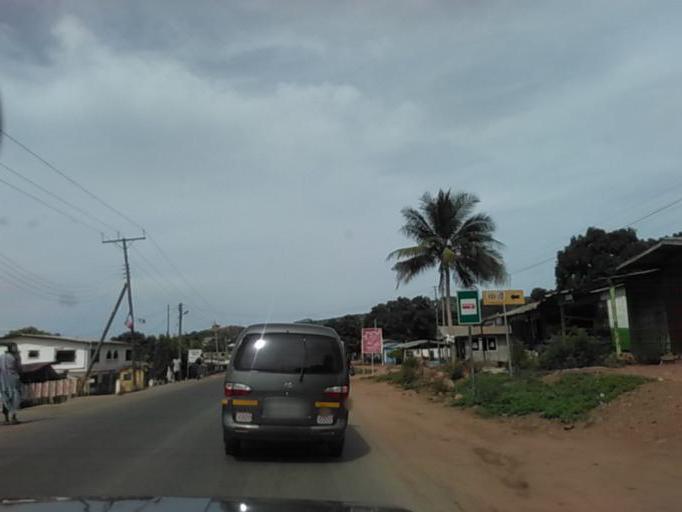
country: GH
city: Akropong
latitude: 6.2306
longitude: 0.0911
